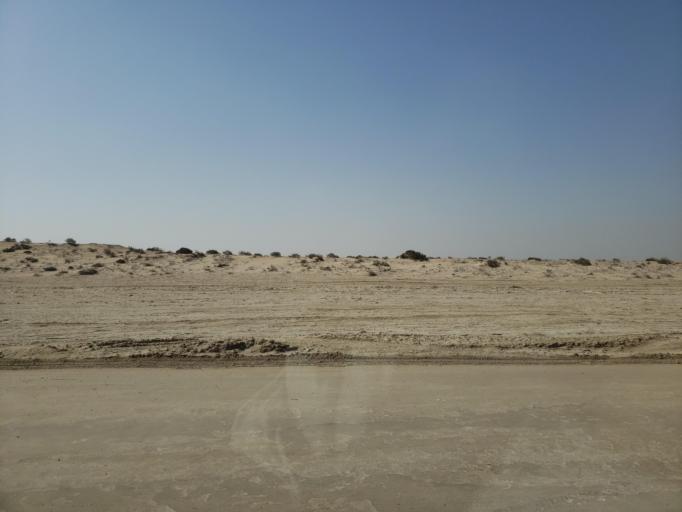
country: AE
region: Umm al Qaywayn
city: Umm al Qaywayn
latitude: 25.5322
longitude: 55.6059
